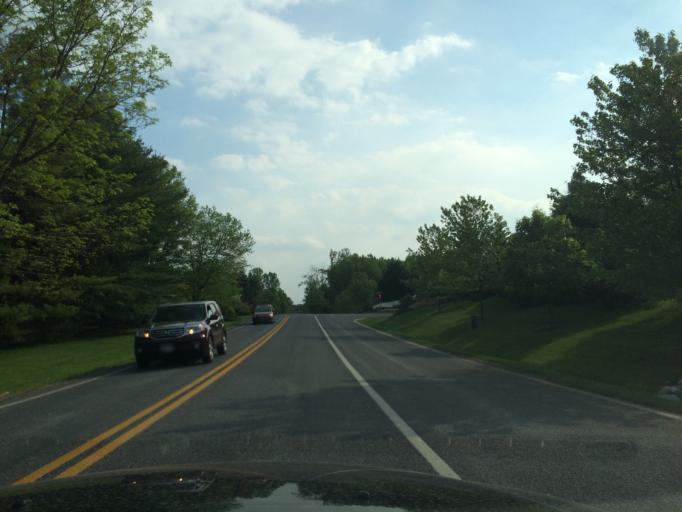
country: US
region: Maryland
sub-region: Howard County
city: Fulton
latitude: 39.1666
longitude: -76.9207
